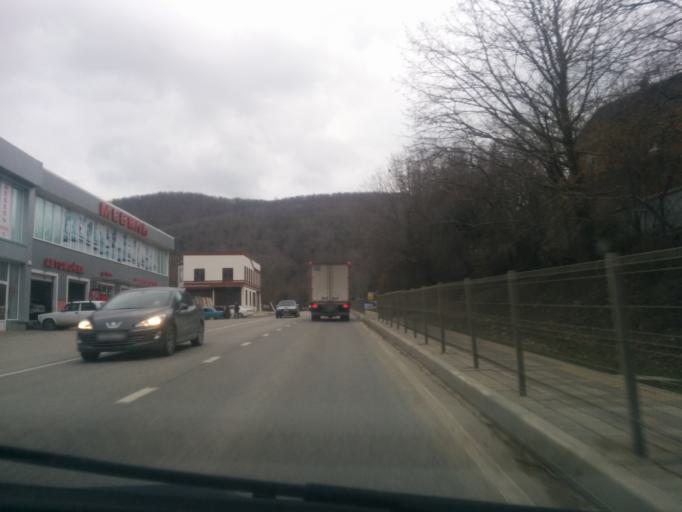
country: RU
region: Krasnodarskiy
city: Novomikhaylovskiy
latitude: 44.2580
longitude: 38.8644
